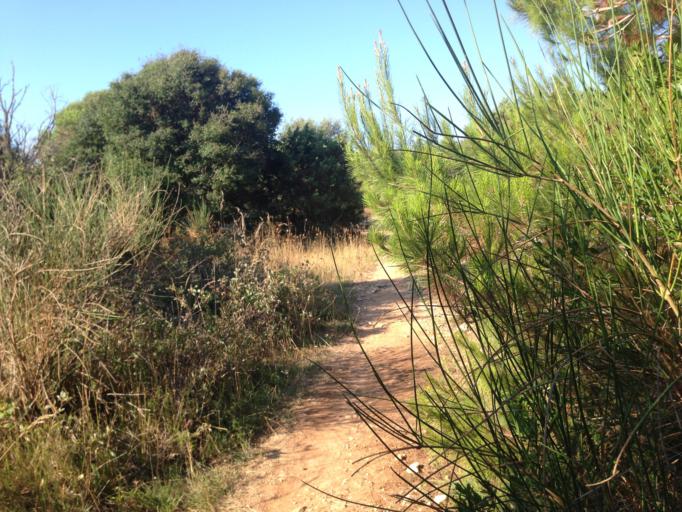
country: HR
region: Istarska
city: Medulin
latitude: 44.7925
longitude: 13.9086
